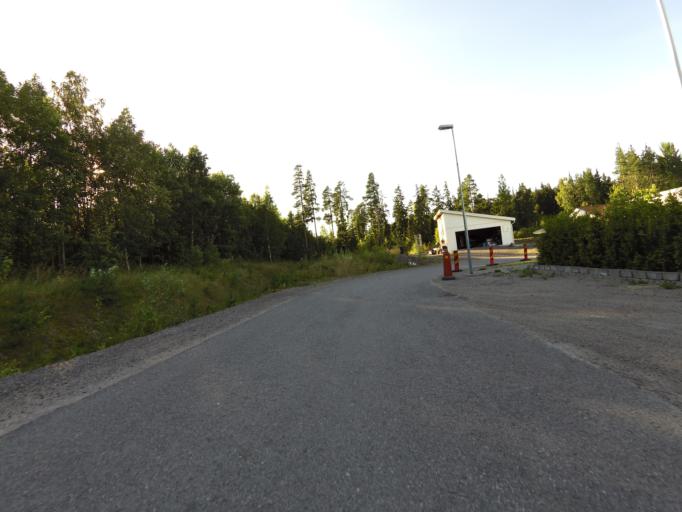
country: SE
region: Gaevleborg
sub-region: Gavle Kommun
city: Gavle
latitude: 60.6437
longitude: 17.1295
